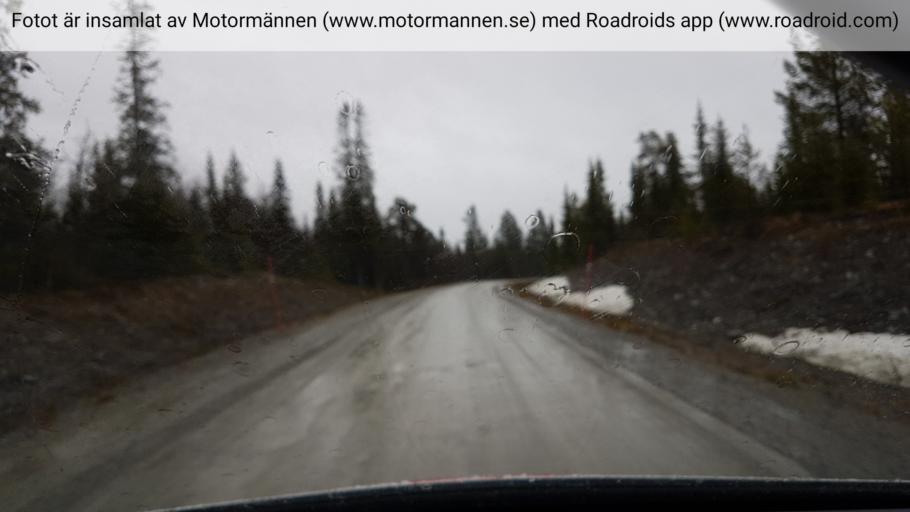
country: SE
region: Jaemtland
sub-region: Are Kommun
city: Are
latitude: 62.6549
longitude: 13.0451
